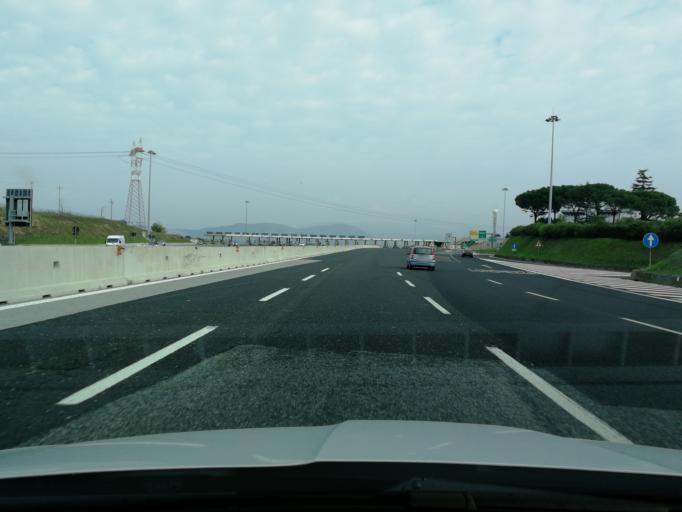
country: IT
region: Latium
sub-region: Citta metropolitana di Roma Capitale
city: Albuccione
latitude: 41.9260
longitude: 12.6997
